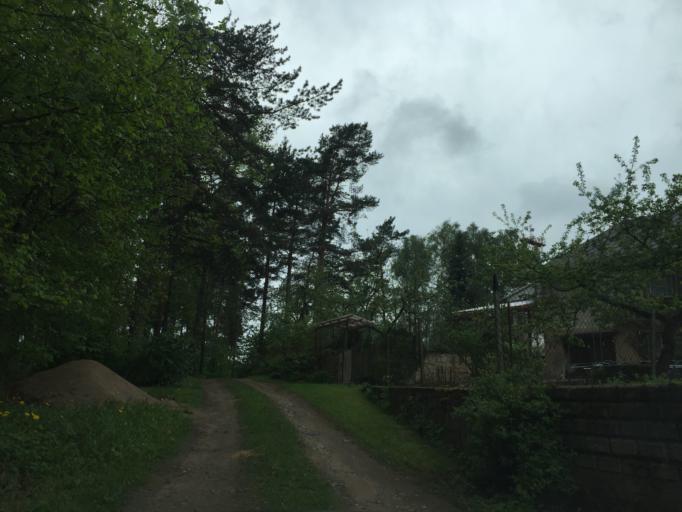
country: LV
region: Kegums
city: Kegums
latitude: 56.7476
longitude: 24.7279
